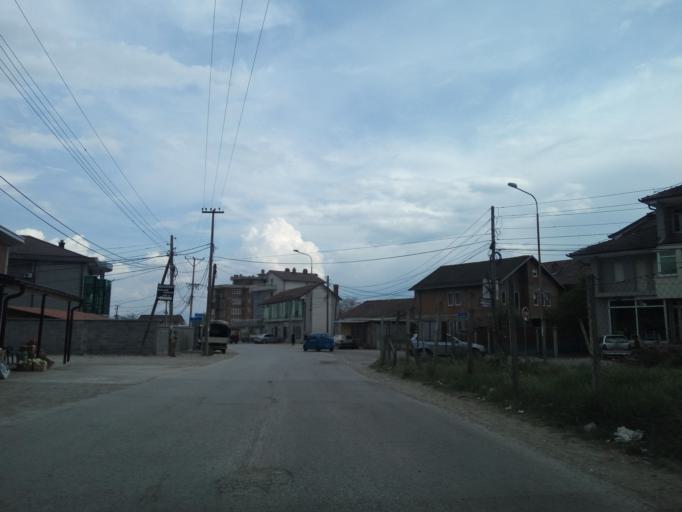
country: XK
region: Gjakova
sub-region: Komuna e Gjakoves
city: Gjakove
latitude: 42.3702
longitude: 20.4165
